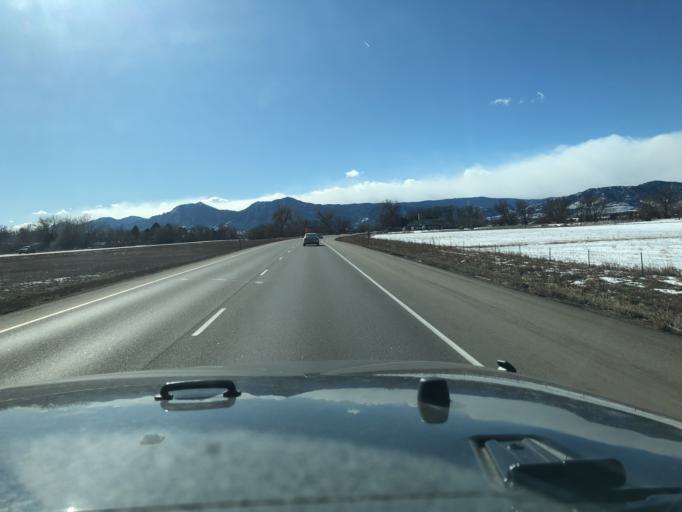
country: US
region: Colorado
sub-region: Boulder County
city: Gunbarrel
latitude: 40.0616
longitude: -105.2210
